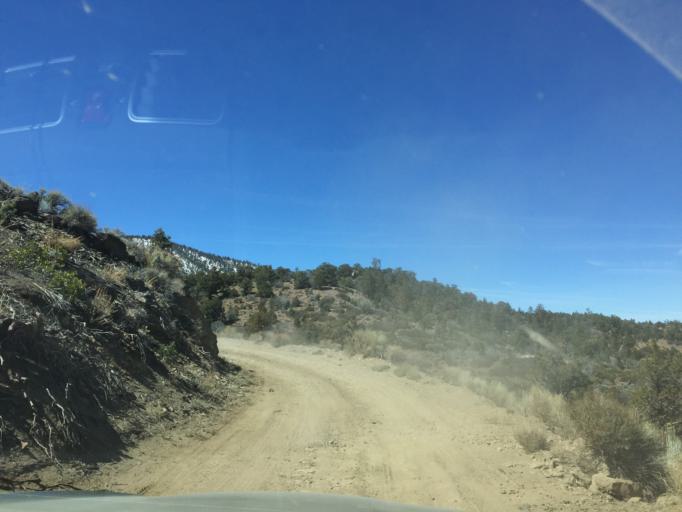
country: US
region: California
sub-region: San Bernardino County
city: Big Bear City
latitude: 34.2140
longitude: -116.7258
